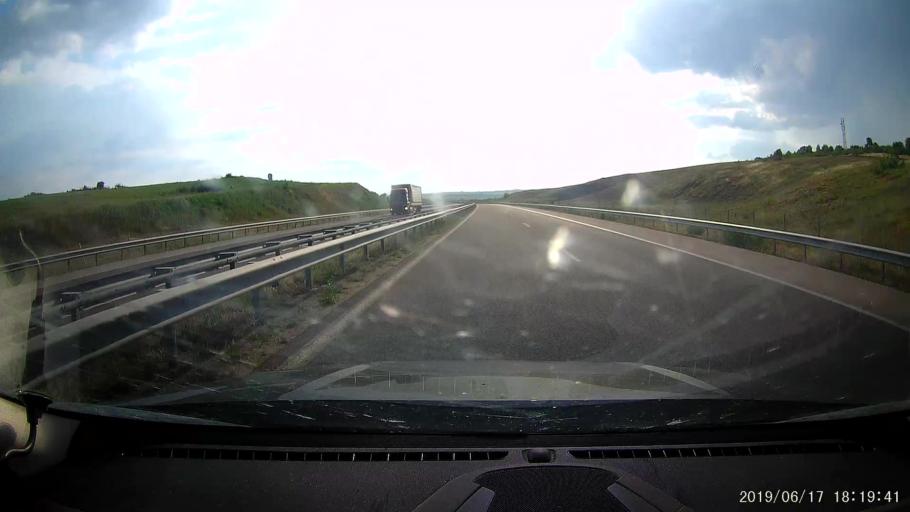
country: BG
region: Khaskovo
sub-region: Obshtina Kharmanli
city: Kharmanli
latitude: 41.9630
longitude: 25.8383
